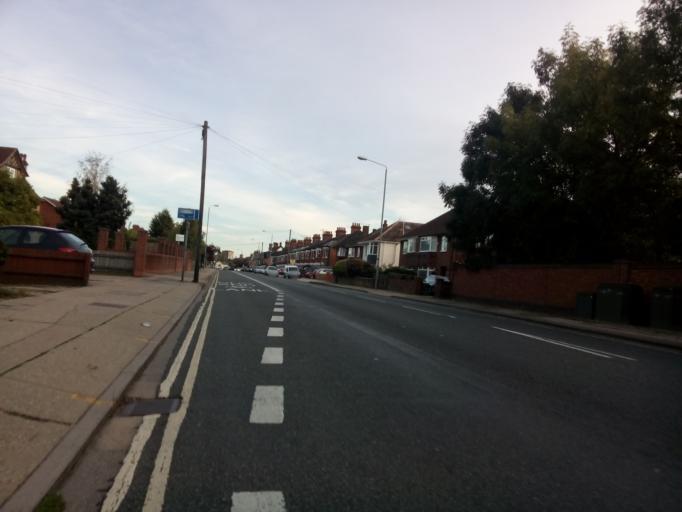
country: GB
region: England
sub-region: Suffolk
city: Ipswich
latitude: 52.0708
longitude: 1.1338
